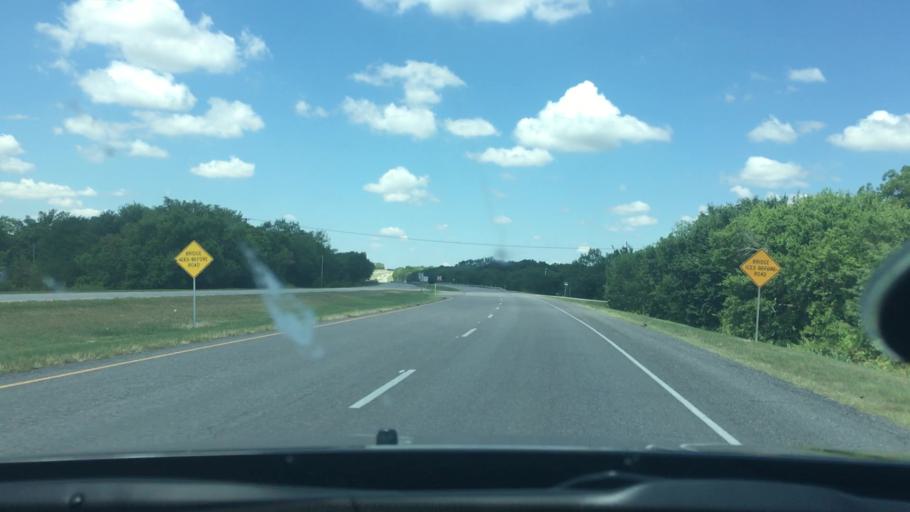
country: US
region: Oklahoma
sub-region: Carter County
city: Wilson
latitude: 34.1740
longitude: -97.3678
